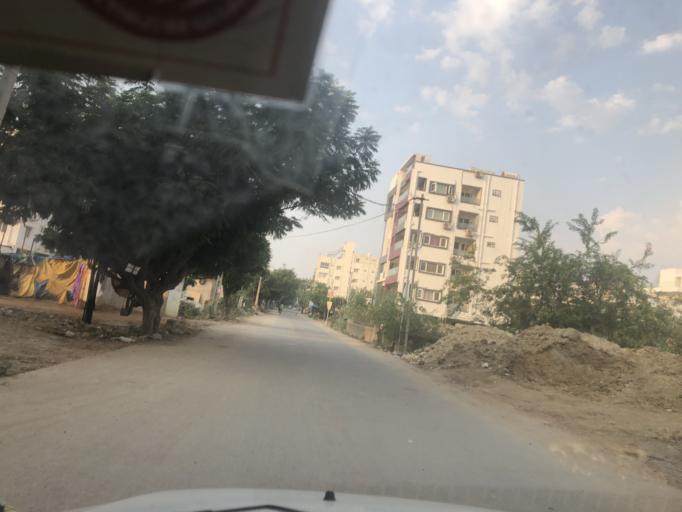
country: IN
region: Telangana
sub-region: Rangareddi
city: Kukatpalli
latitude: 17.4454
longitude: 78.3991
